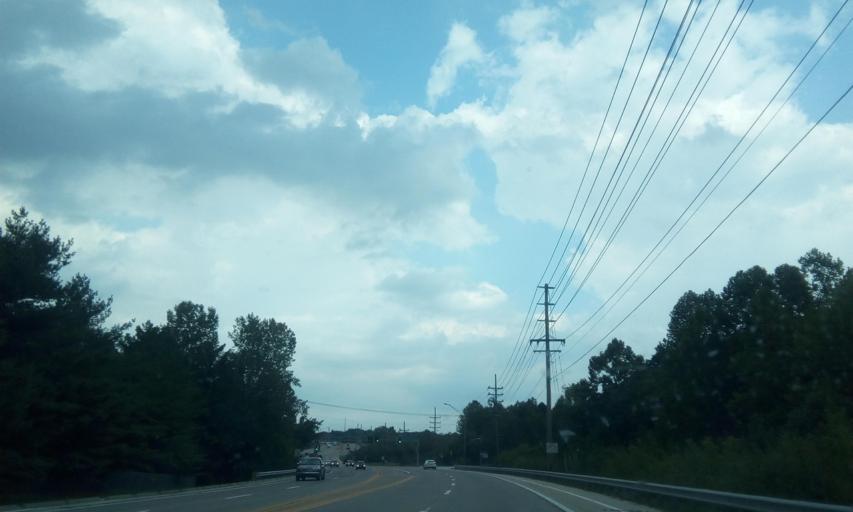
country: US
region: Missouri
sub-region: Saint Louis County
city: Des Peres
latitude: 38.5799
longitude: -90.4558
